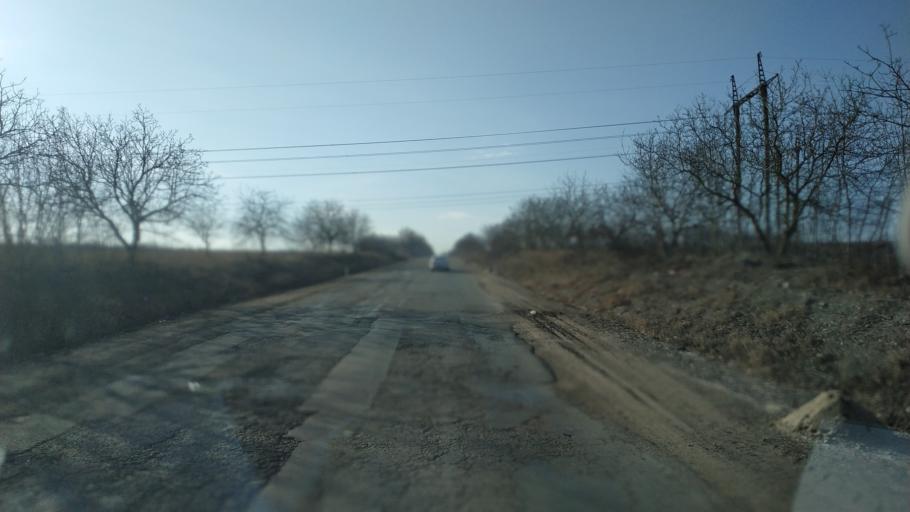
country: MD
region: Chisinau
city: Singera
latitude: 46.8746
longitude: 29.0396
